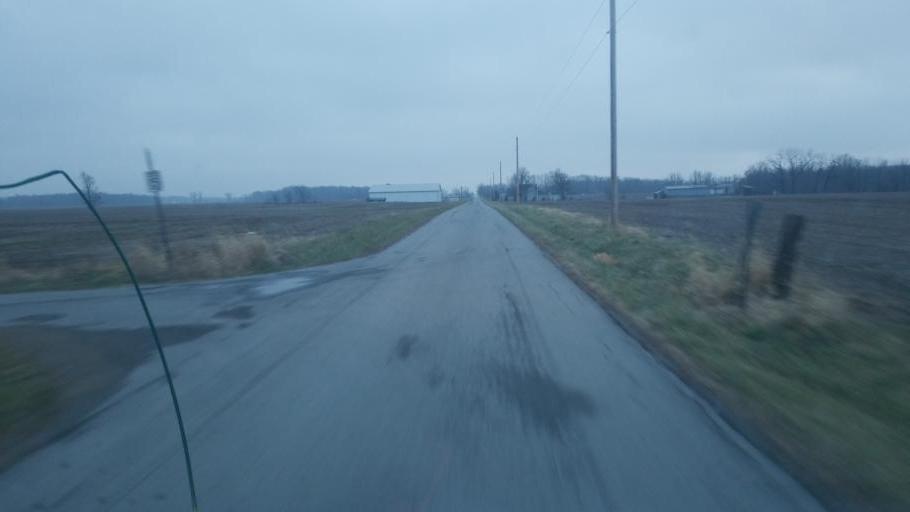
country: US
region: Ohio
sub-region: Seneca County
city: Tiffin
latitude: 40.9718
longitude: -83.1318
